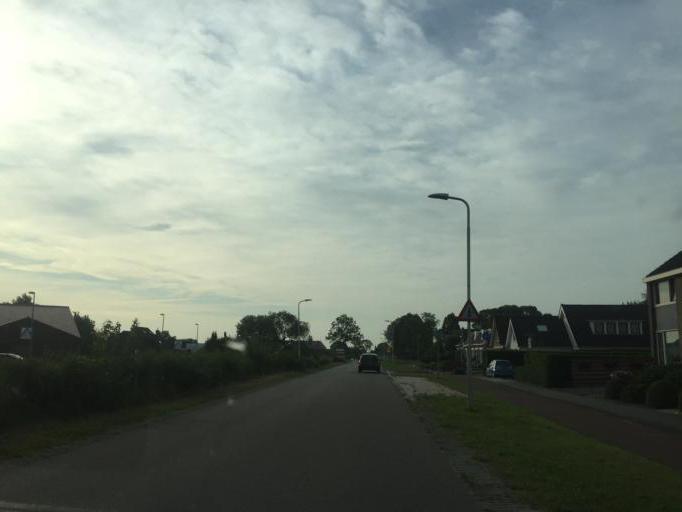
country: NL
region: Friesland
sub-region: Gemeente Dongeradeel
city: Dokkum
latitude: 53.3239
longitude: 6.0049
